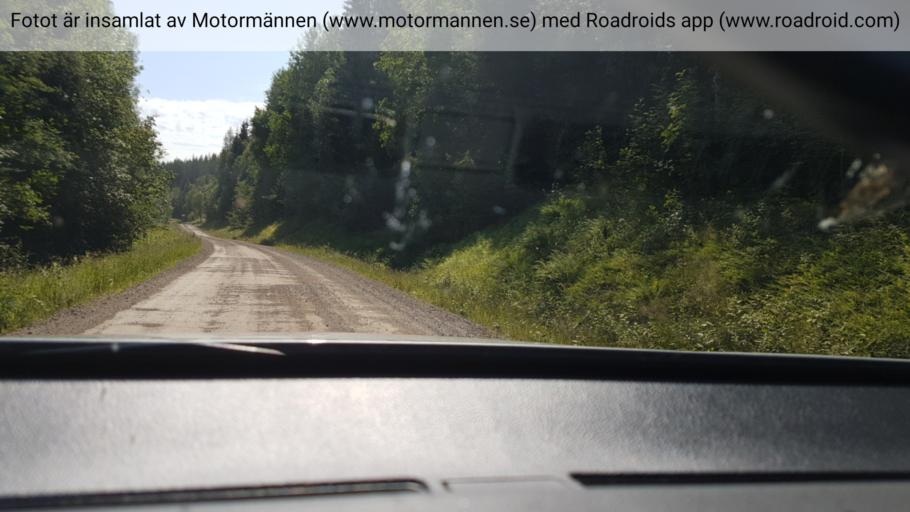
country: SE
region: Vaermland
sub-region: Torsby Kommun
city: Torsby
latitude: 60.4353
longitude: 13.2298
